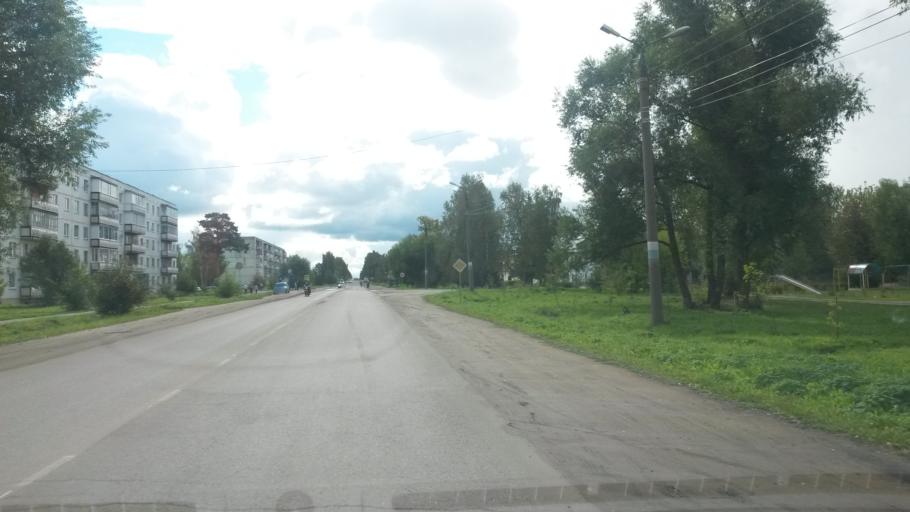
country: RU
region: Ivanovo
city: Zavolzhsk
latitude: 57.4830
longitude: 42.1465
